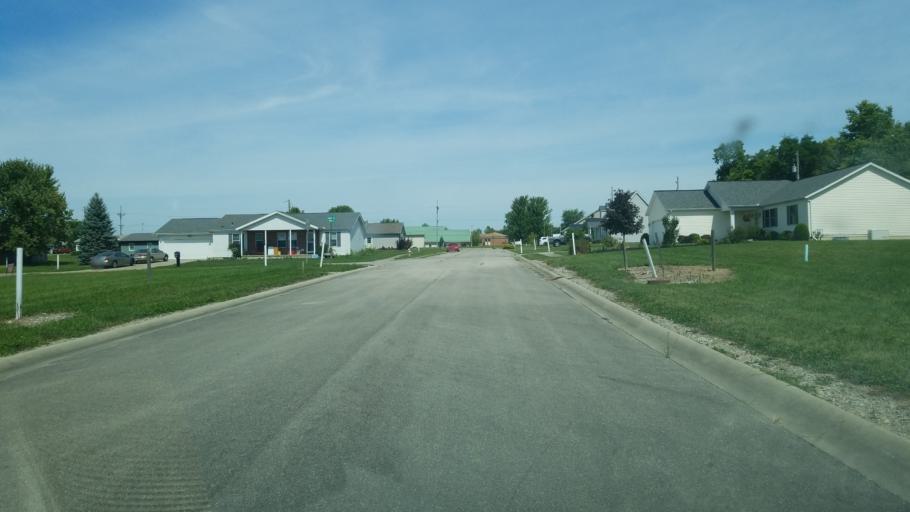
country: US
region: Ohio
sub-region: Hardin County
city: Kenton
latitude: 40.6414
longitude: -83.5946
